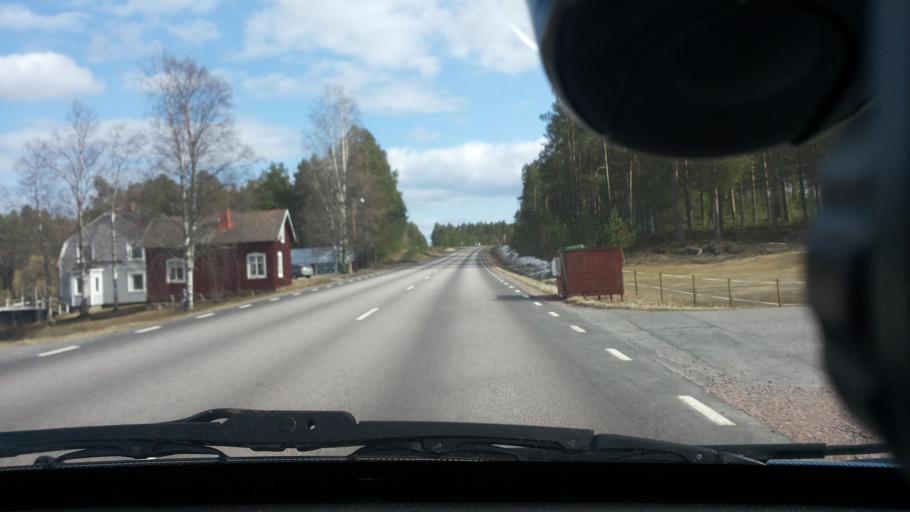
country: SE
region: Norrbotten
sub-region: Lulea Kommun
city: Sodra Sunderbyn
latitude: 65.6377
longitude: 21.9102
